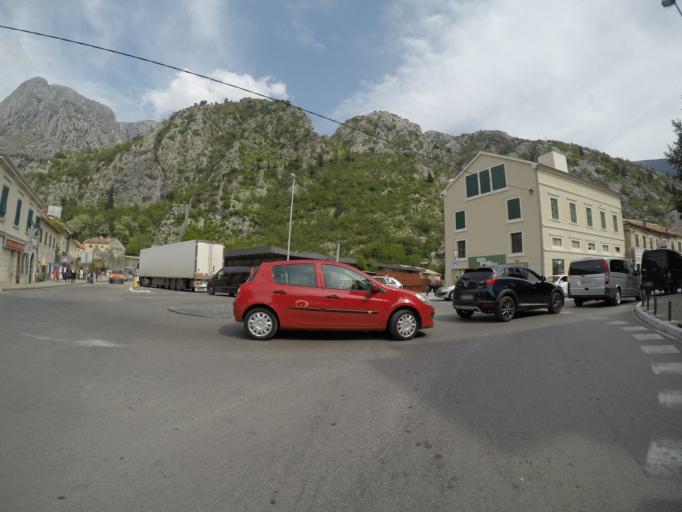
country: ME
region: Kotor
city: Kotor
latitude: 42.4215
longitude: 18.7696
